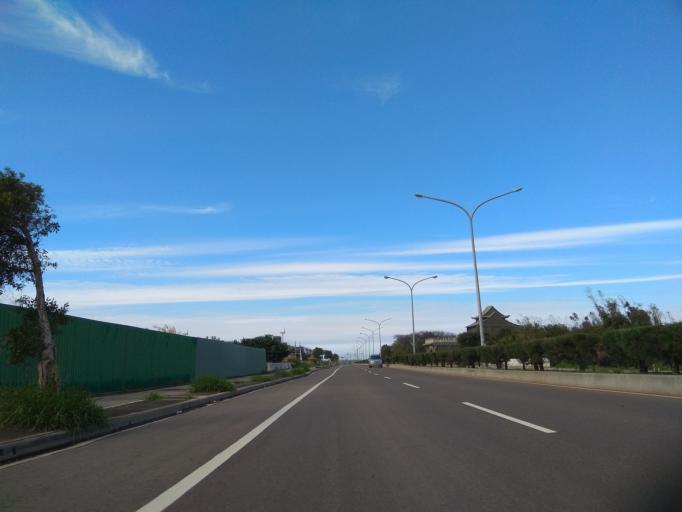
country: TW
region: Taiwan
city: Taoyuan City
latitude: 25.0746
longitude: 121.1718
